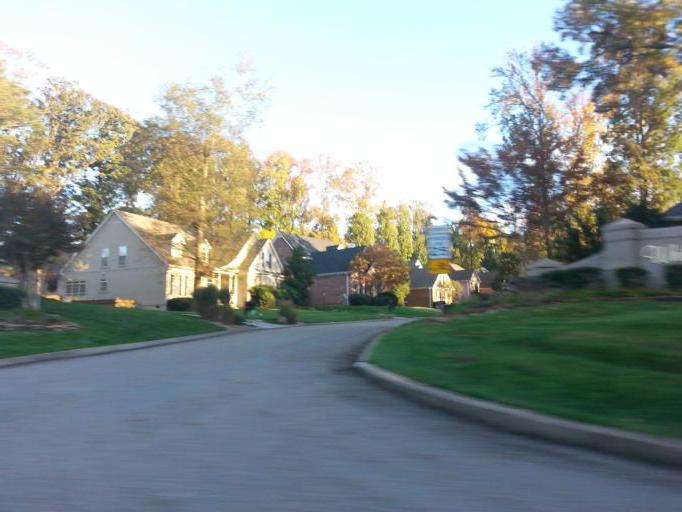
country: US
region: Tennessee
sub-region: Blount County
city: Louisville
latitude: 35.9065
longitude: -84.0447
